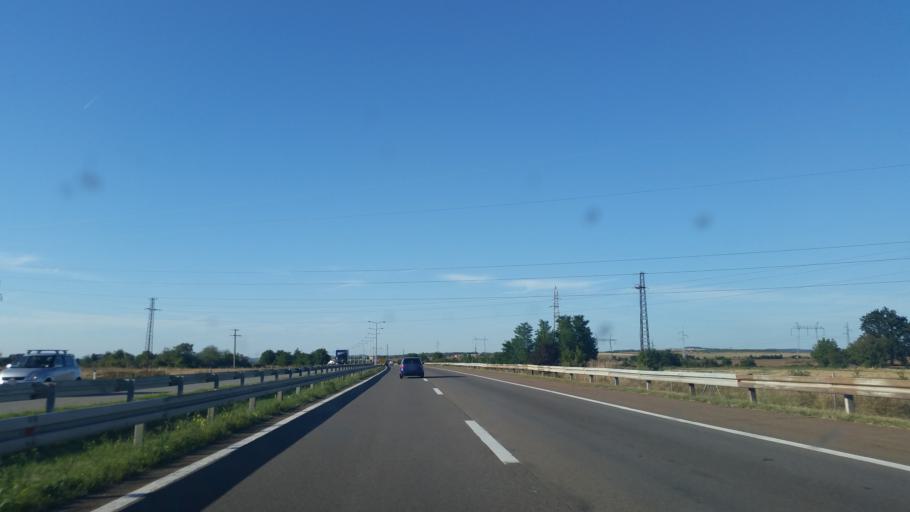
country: RS
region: Central Serbia
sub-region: Pomoravski Okrug
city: Cuprija
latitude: 43.9272
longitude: 21.3920
